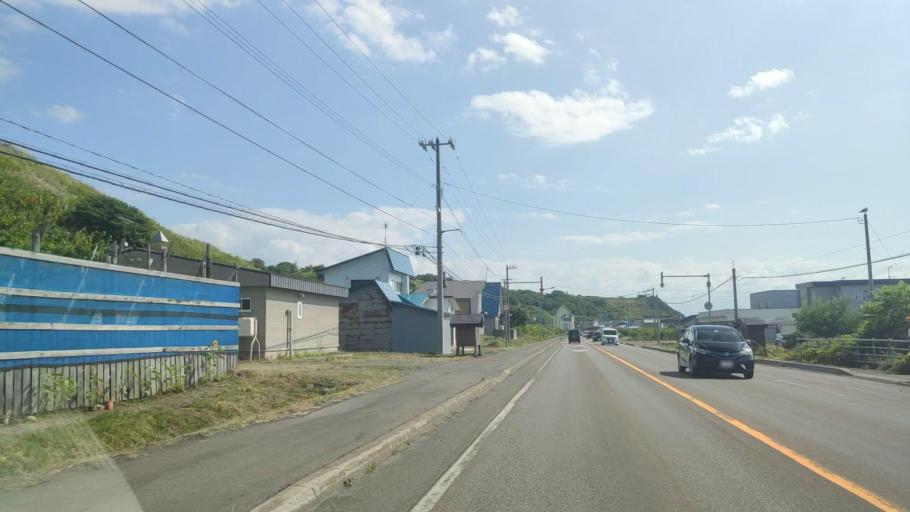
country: JP
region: Hokkaido
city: Rumoi
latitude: 43.9685
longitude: 141.6465
